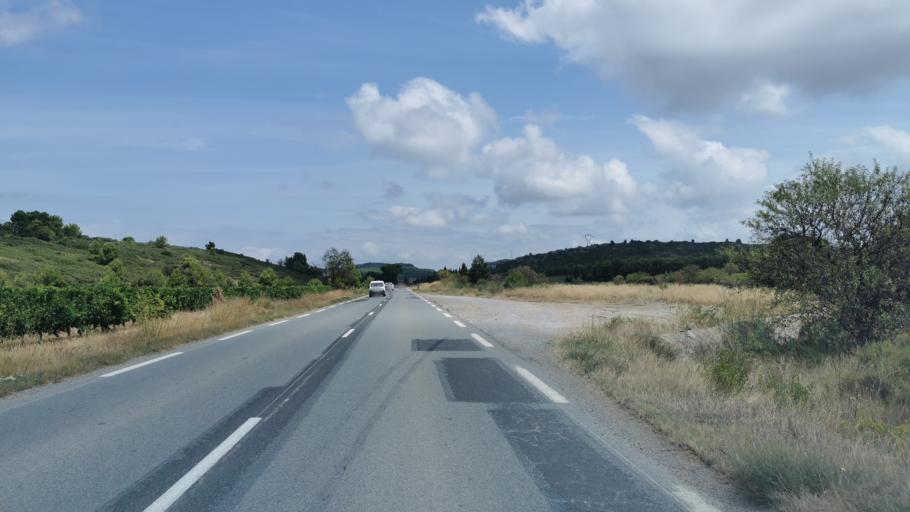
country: FR
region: Languedoc-Roussillon
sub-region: Departement de l'Aude
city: Nevian
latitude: 43.1743
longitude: 2.9280
